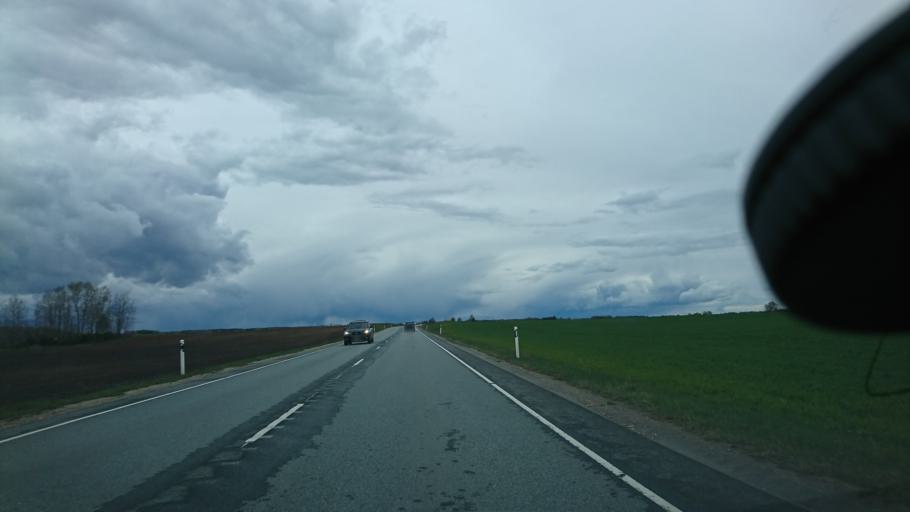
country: EE
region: Laeaene-Virumaa
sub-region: Haljala vald
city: Haljala
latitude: 59.3487
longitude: 26.2594
